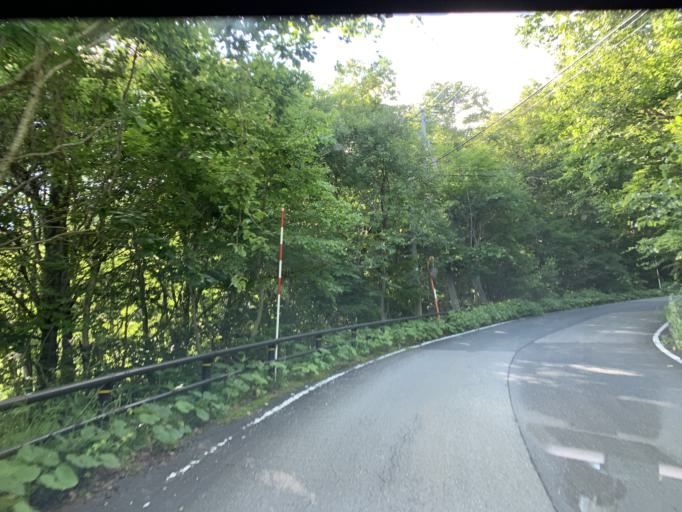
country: JP
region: Iwate
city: Ichinoseki
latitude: 38.9168
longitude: 140.8282
